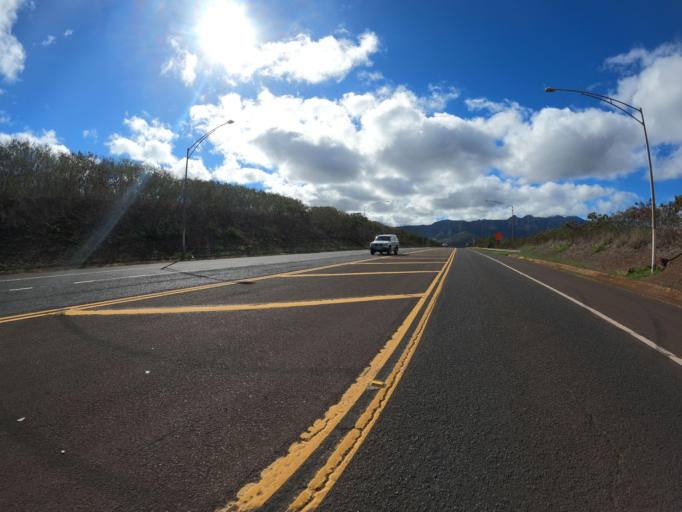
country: US
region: Hawaii
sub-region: Honolulu County
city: Hale'iwa
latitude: 21.5888
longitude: -158.1013
